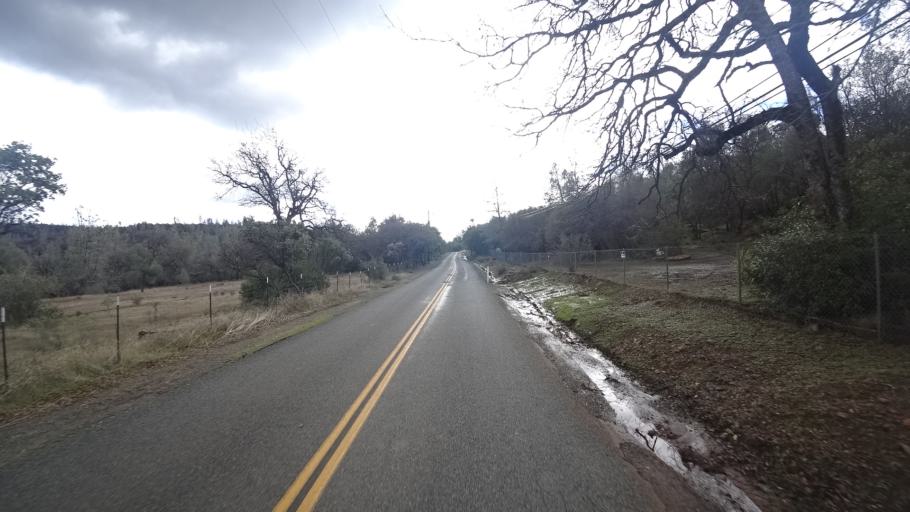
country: US
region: California
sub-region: Butte County
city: Berry Creek
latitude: 39.6377
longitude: -121.5281
